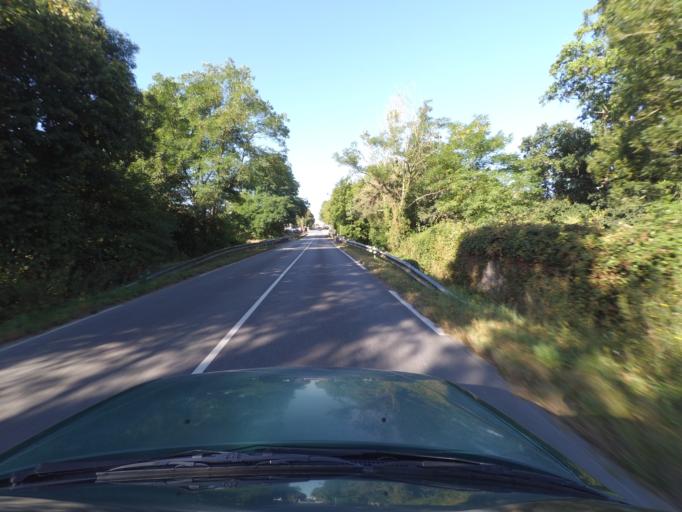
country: FR
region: Pays de la Loire
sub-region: Departement de la Loire-Atlantique
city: Les Sorinieres
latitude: 47.1218
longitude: -1.5315
